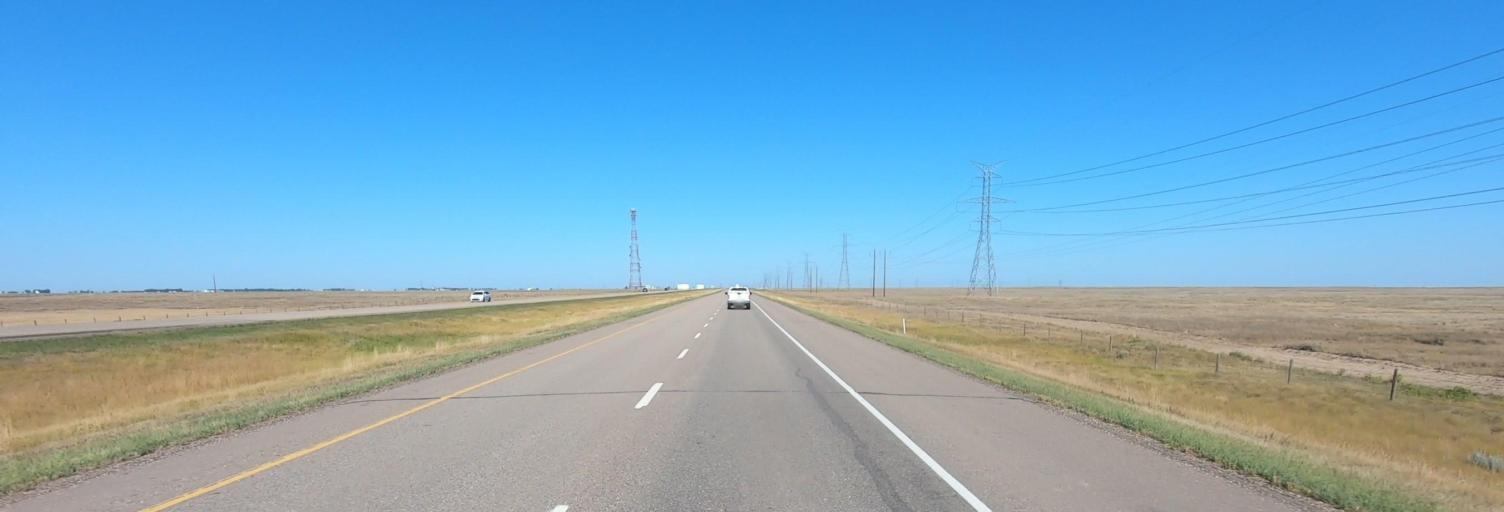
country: CA
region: Alberta
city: Brooks
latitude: 50.4397
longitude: -111.5554
